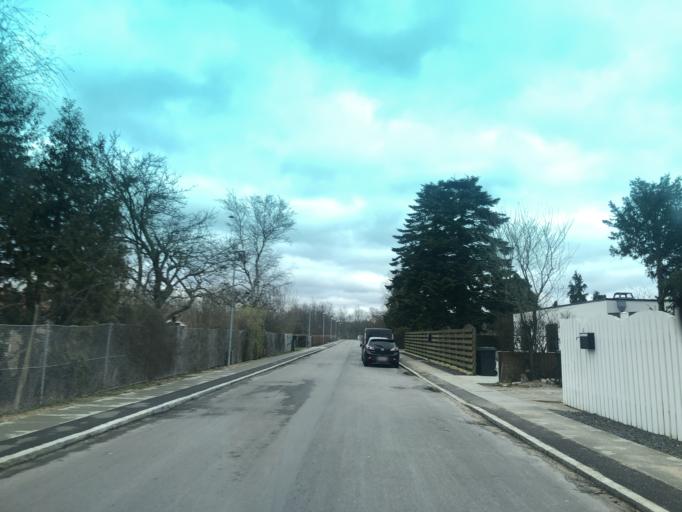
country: DK
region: Capital Region
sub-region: Tarnby Kommune
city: Tarnby
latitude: 55.6021
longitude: 12.5863
